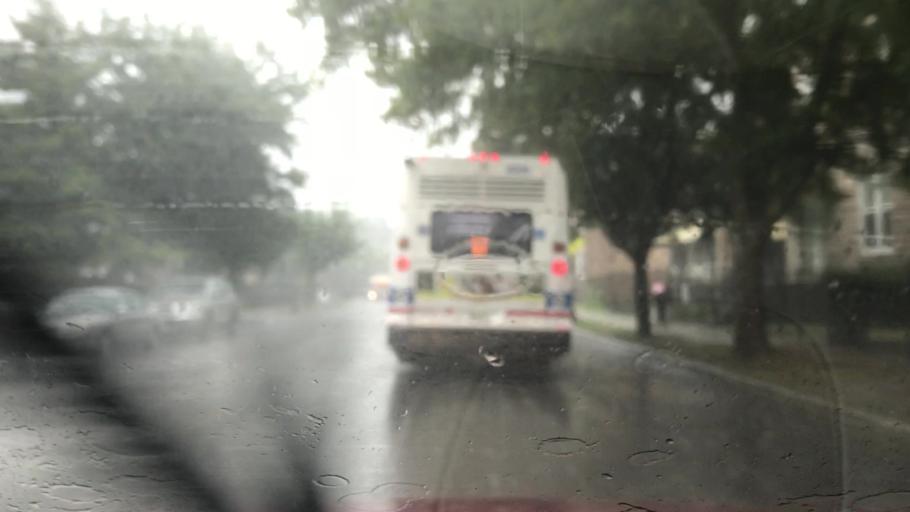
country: US
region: Illinois
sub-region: Cook County
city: Oak Park
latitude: 41.8847
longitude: -87.7552
